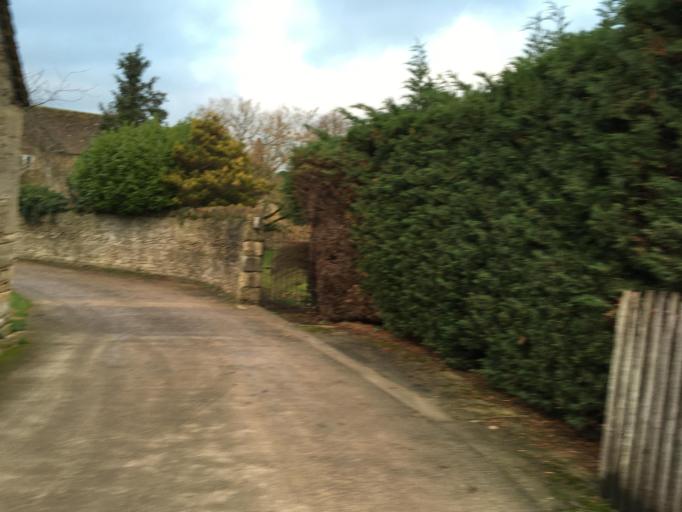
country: GB
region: England
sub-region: Wiltshire
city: Lacock
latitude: 51.4147
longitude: -2.1207
